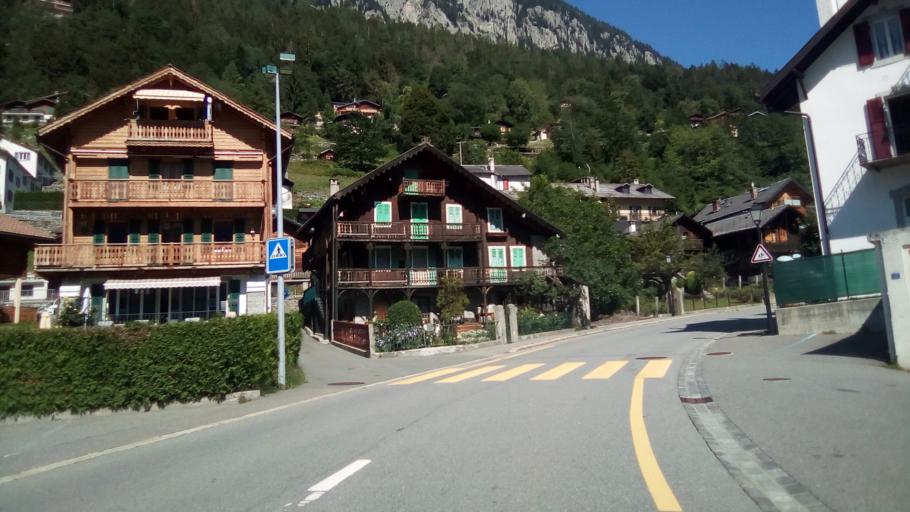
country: CH
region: Valais
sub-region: Saint-Maurice District
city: Salvan
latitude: 46.1190
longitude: 7.0196
